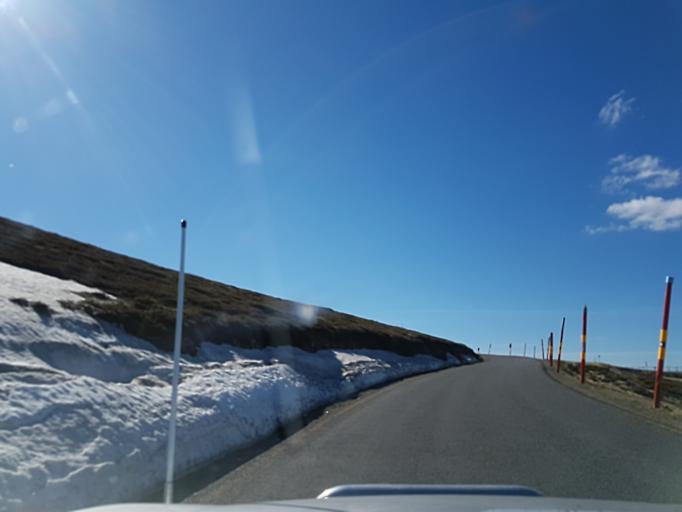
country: AU
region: Victoria
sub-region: Alpine
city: Mount Beauty
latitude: -36.9763
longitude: 147.1387
